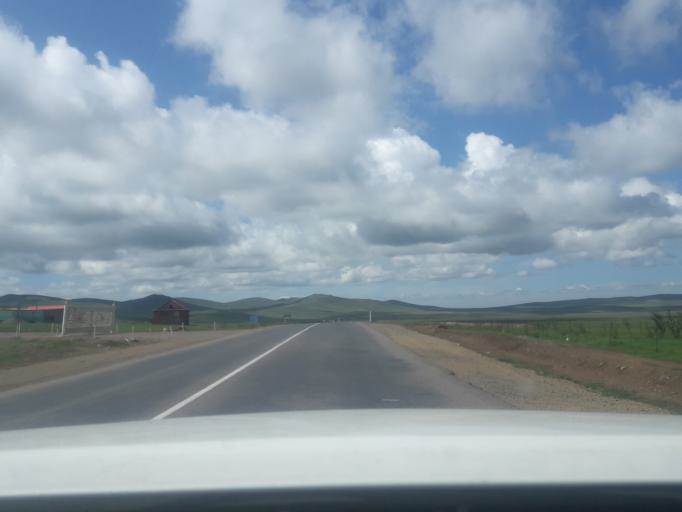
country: MN
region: Central Aimak
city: Altanbulag
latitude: 47.9008
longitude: 106.4760
